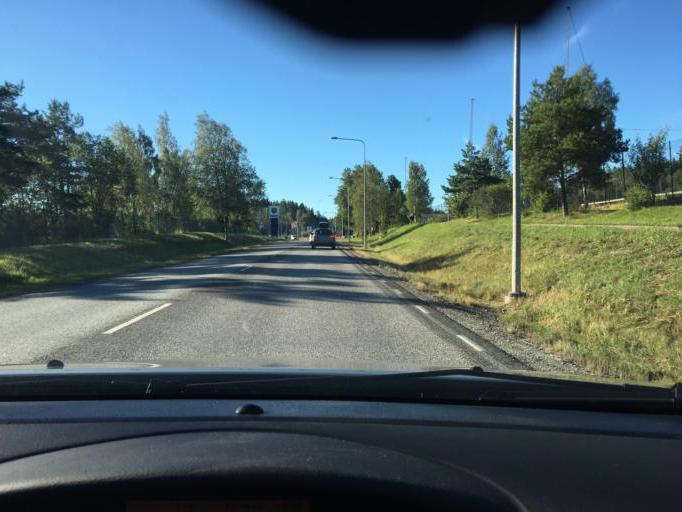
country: SE
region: Stockholm
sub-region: Sodertalje Kommun
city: Pershagen
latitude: 59.1677
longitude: 17.6391
